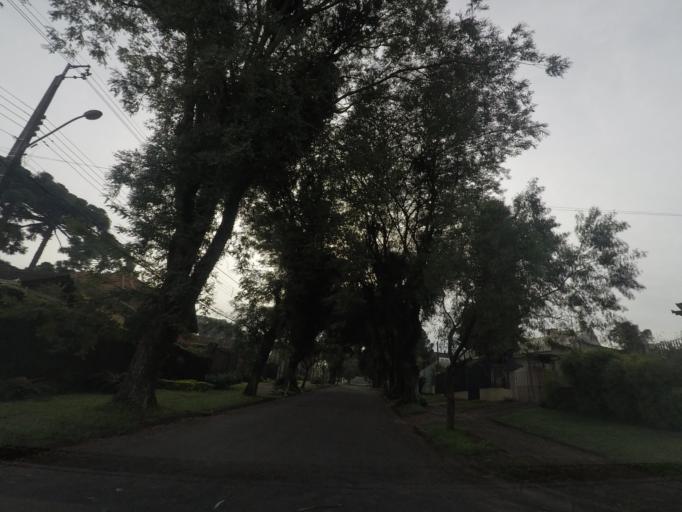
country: BR
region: Parana
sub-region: Curitiba
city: Curitiba
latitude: -25.4377
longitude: -49.2992
